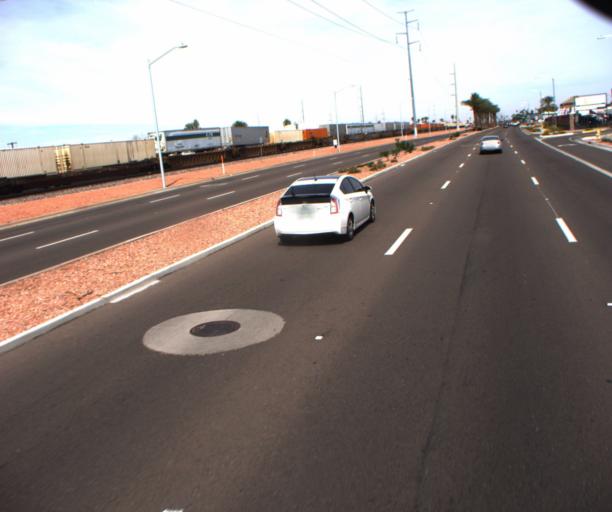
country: US
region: Arizona
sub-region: Maricopa County
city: Glendale
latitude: 33.5331
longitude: -112.1794
